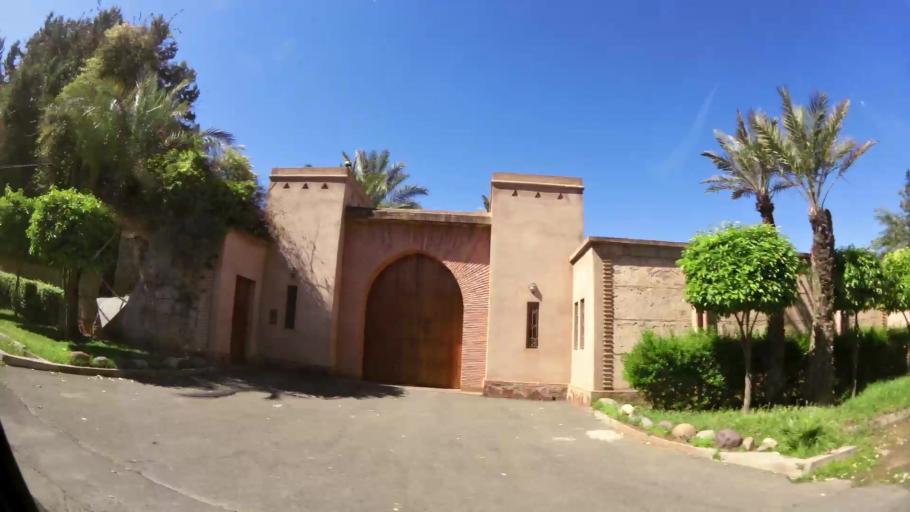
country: MA
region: Marrakech-Tensift-Al Haouz
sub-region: Marrakech
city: Marrakesh
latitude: 31.6531
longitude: -7.9711
